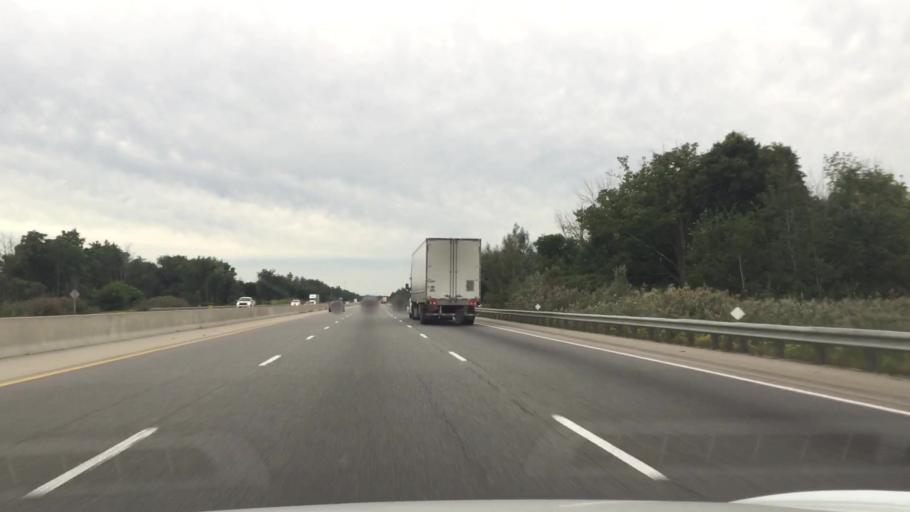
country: CA
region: Ontario
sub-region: Oxford County
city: Woodstock
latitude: 43.1996
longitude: -80.6316
